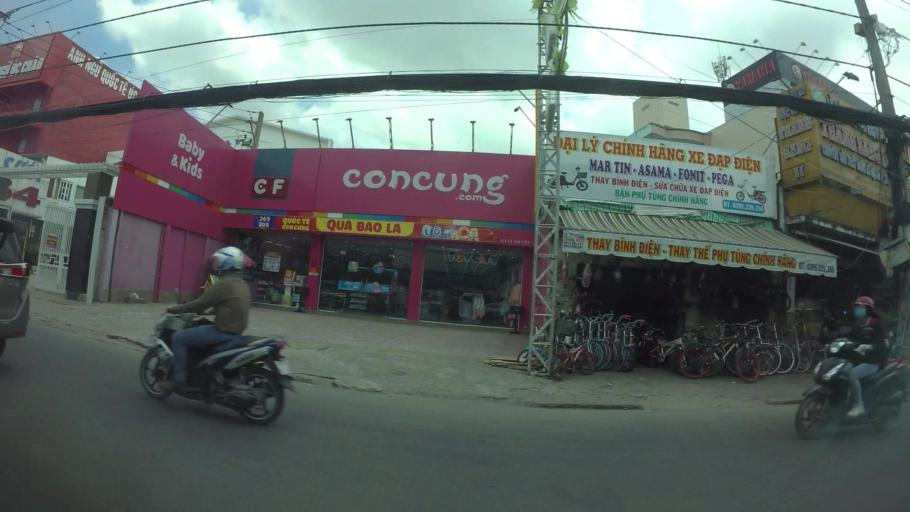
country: VN
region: Ho Chi Minh City
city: Thu Duc
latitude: 10.8438
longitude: 106.7812
